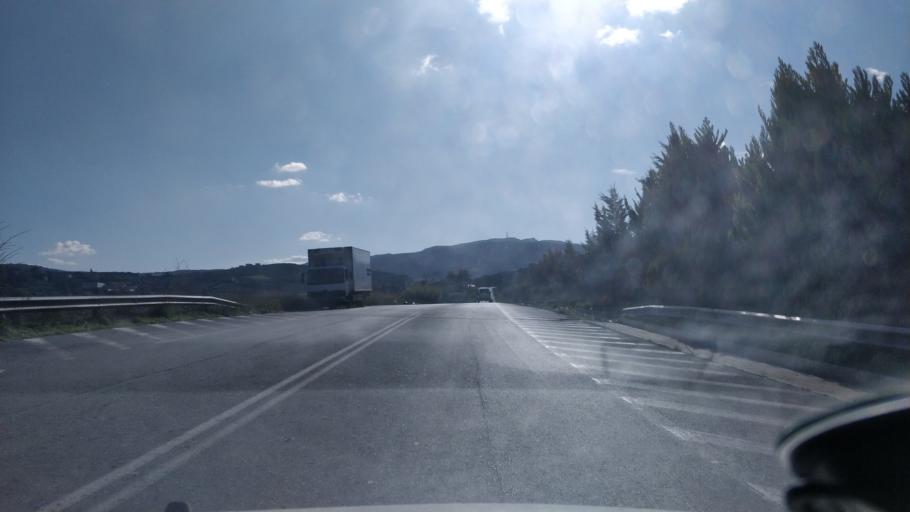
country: GR
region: Crete
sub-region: Nomos Irakleiou
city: Ano Arhanes
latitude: 35.2176
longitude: 25.1980
